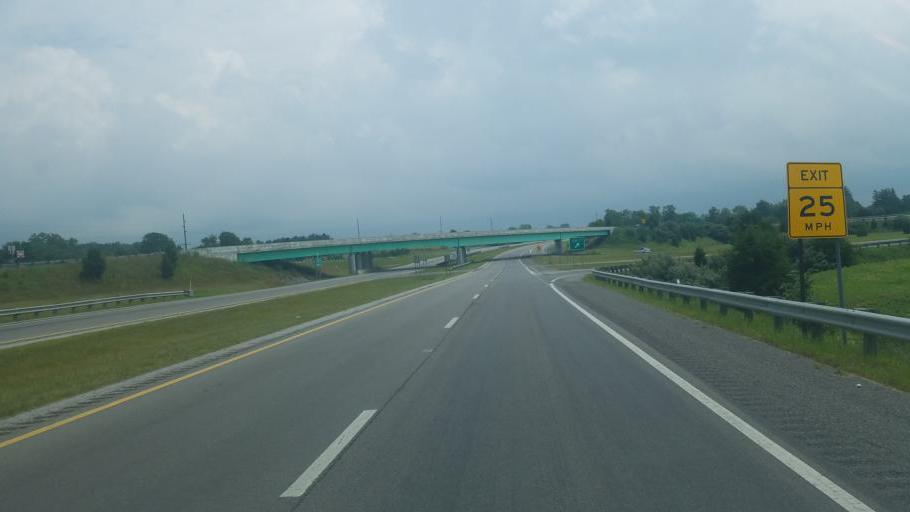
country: US
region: Ohio
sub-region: Logan County
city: Northwood
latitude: 40.4353
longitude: -83.8059
